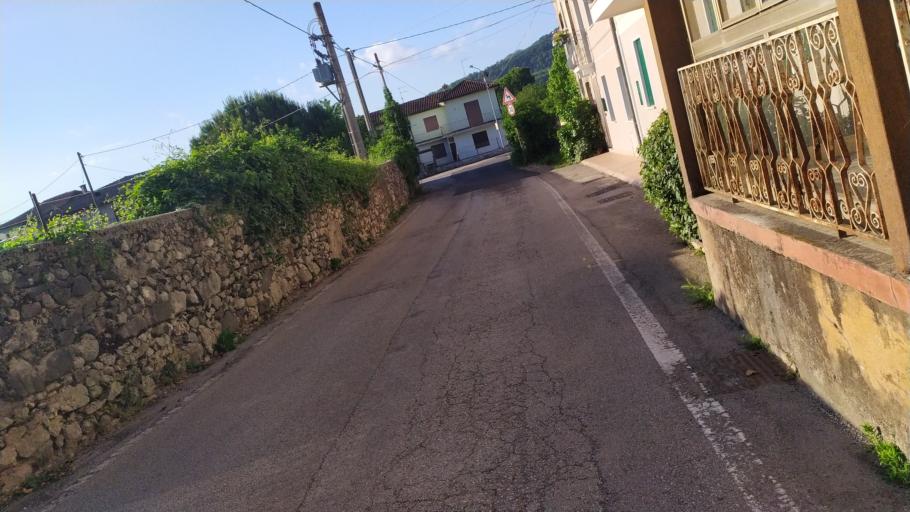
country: IT
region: Veneto
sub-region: Provincia di Vicenza
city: Isola Vicentina
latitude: 45.6336
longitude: 11.4242
